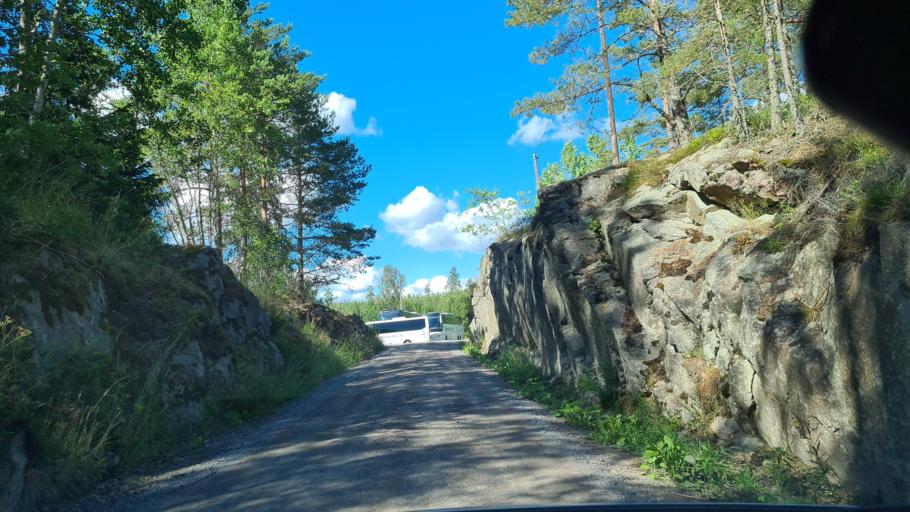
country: SE
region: OEstergoetland
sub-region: Norrkopings Kommun
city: Krokek
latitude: 58.6784
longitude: 16.4289
